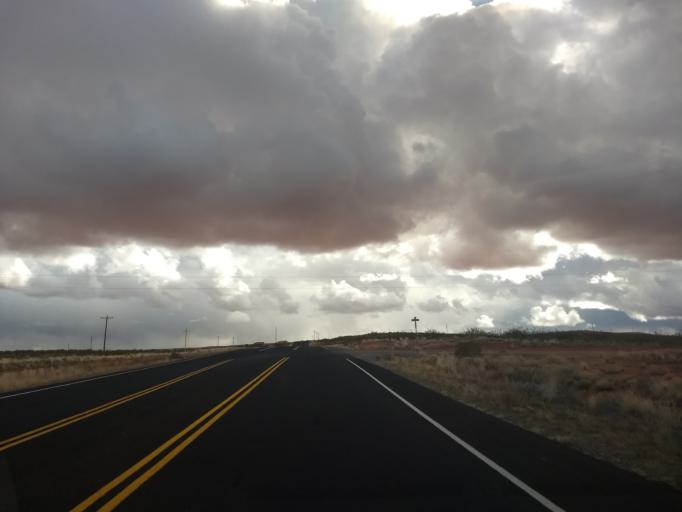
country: US
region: Utah
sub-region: Washington County
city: Hurricane
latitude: 37.1453
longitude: -113.3897
